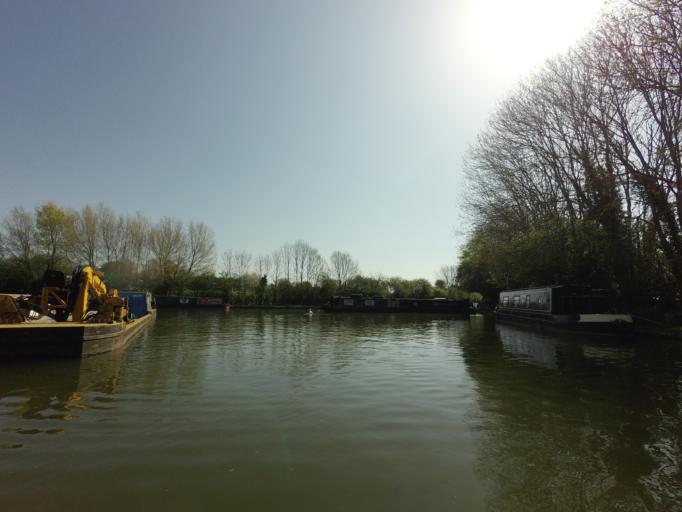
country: GB
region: England
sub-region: Buckinghamshire
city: Cheddington
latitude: 51.8206
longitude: -0.6701
